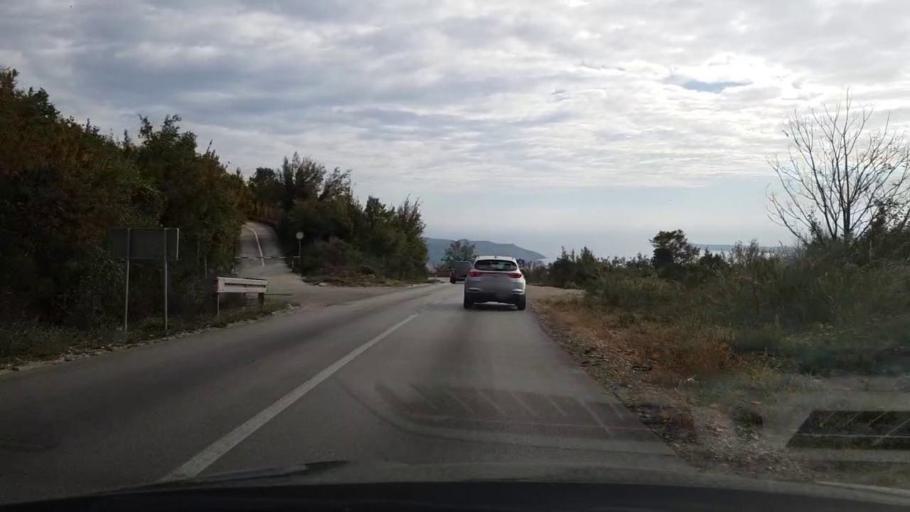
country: ME
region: Herceg Novi
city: Herceg-Novi
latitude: 42.4709
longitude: 18.5372
